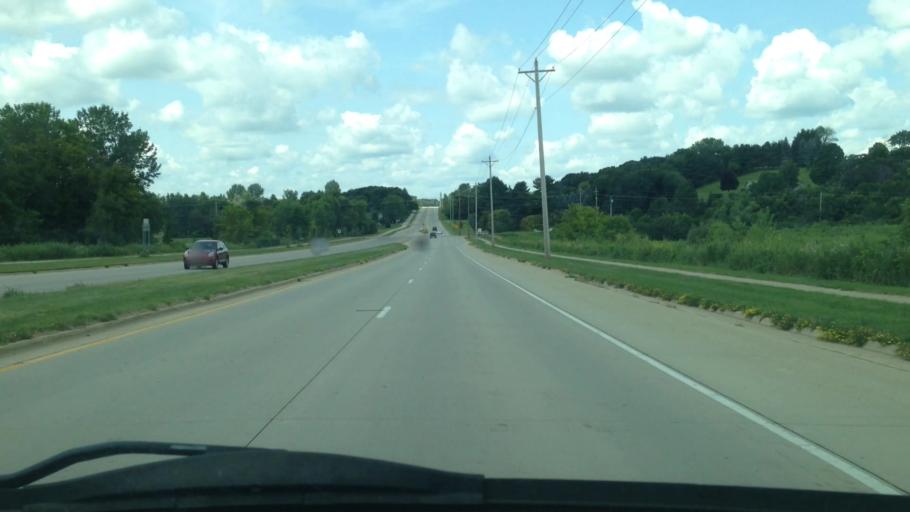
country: US
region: Minnesota
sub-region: Olmsted County
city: Rochester
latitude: 43.9531
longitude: -92.4743
